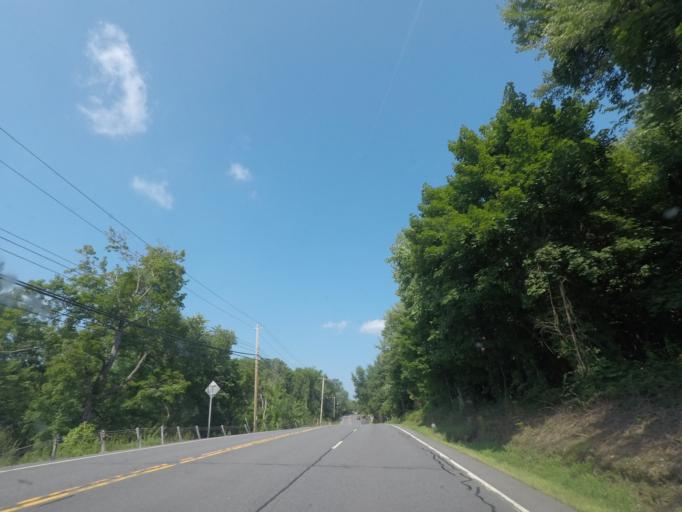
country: US
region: New York
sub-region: Rensselaer County
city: Nassau
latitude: 42.5151
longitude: -73.5959
